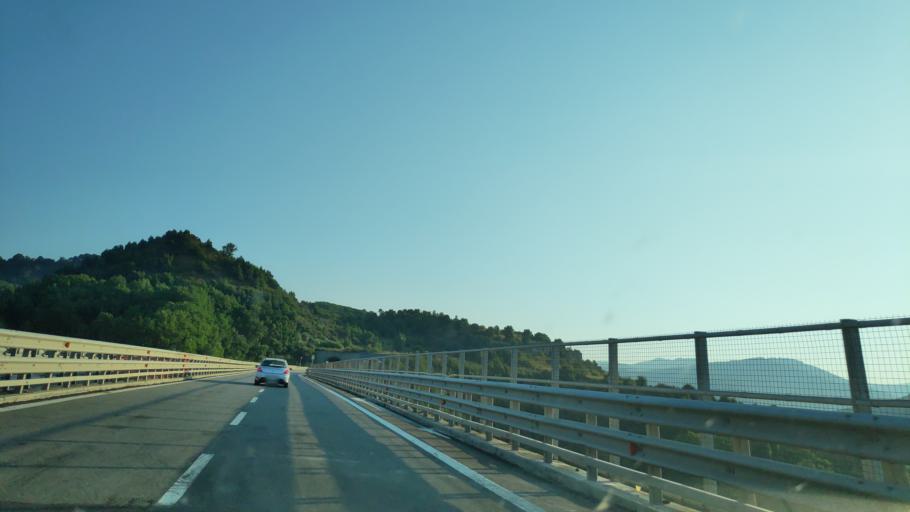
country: IT
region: Calabria
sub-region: Provincia di Cosenza
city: Carpanzano
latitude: 39.1500
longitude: 16.2831
